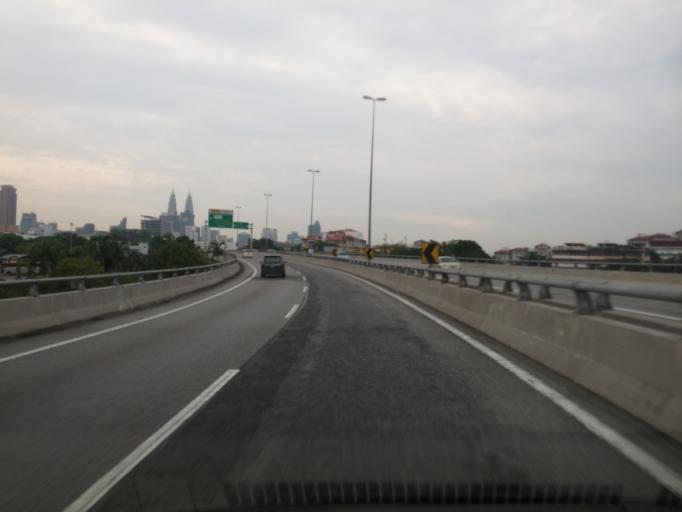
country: MY
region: Kuala Lumpur
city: Kuala Lumpur
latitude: 3.1273
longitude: 101.7189
